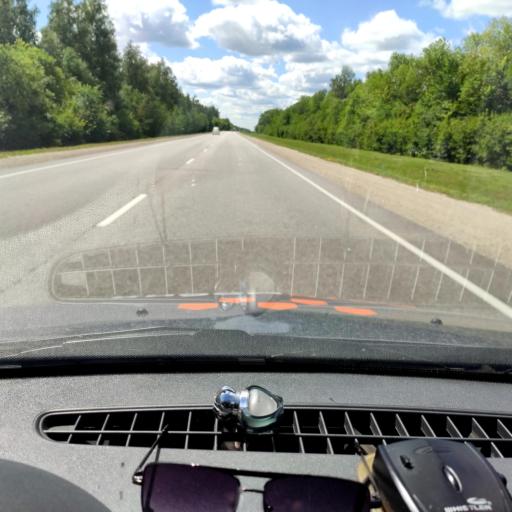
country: RU
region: Lipetsk
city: Borinskoye
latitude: 52.3981
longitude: 39.2354
